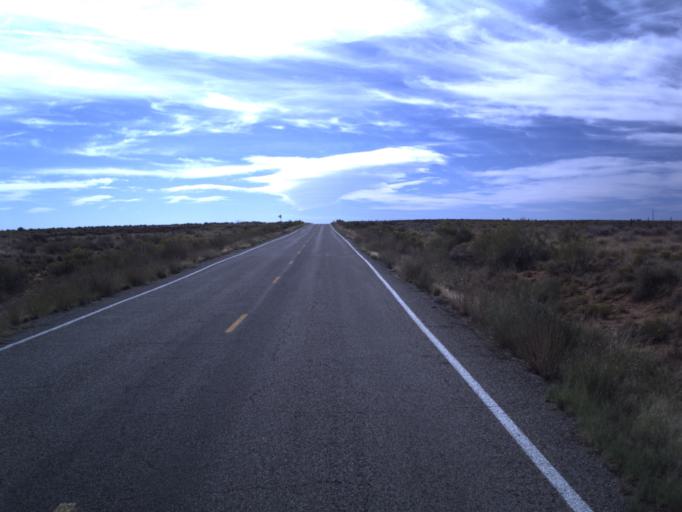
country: US
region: Utah
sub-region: San Juan County
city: Blanding
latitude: 37.3338
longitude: -109.3470
